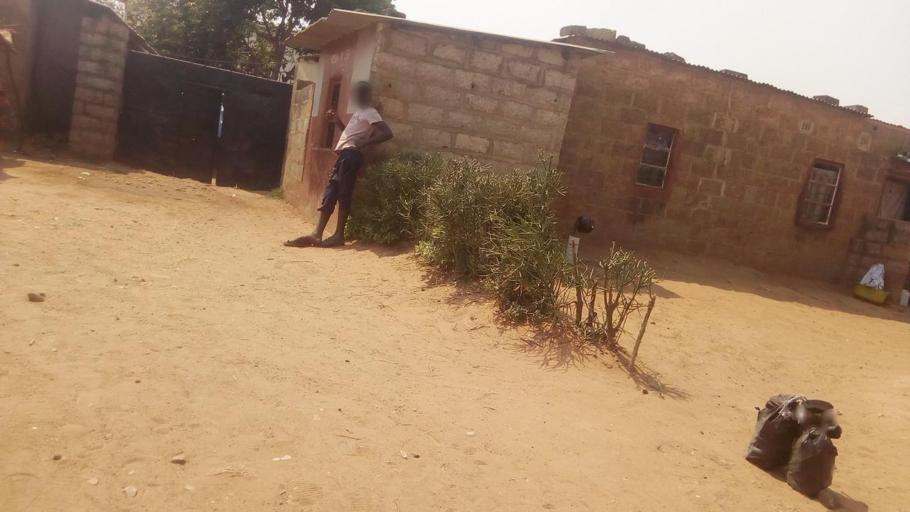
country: ZM
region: Lusaka
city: Lusaka
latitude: -15.3595
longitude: 28.2941
